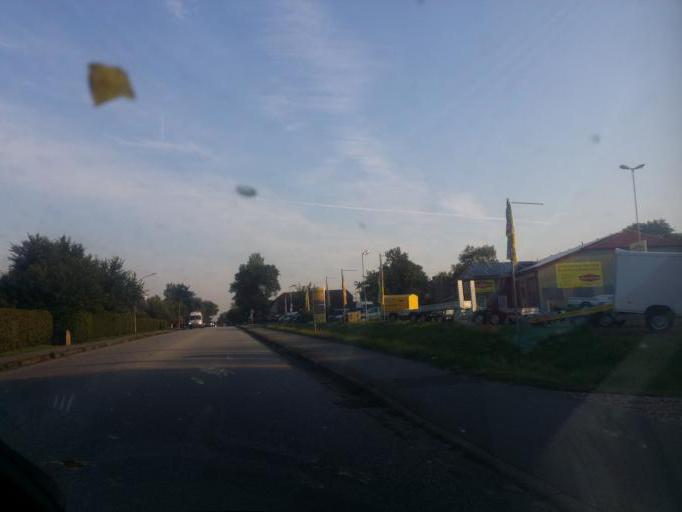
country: DE
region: Schleswig-Holstein
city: Breklum
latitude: 54.5977
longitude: 8.9879
